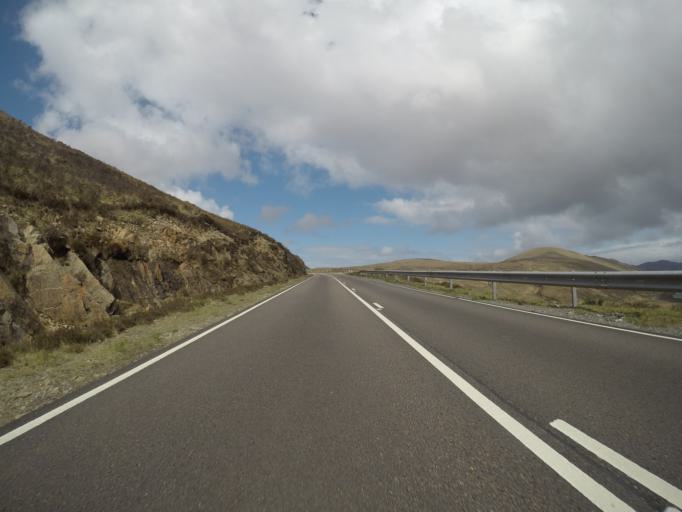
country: GB
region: Scotland
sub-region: Highland
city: Portree
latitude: 57.2714
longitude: -6.0897
